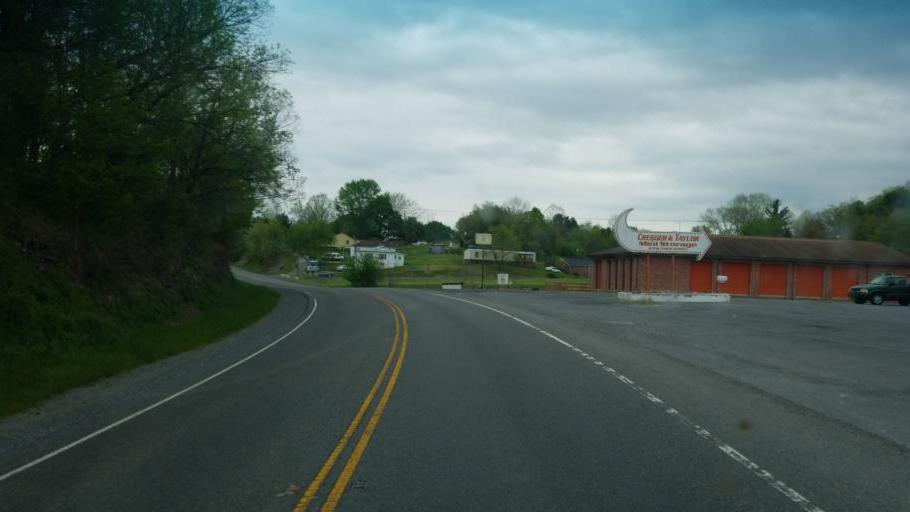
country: US
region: Virginia
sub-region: Smyth County
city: Adwolf
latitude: 36.8153
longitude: -81.5631
